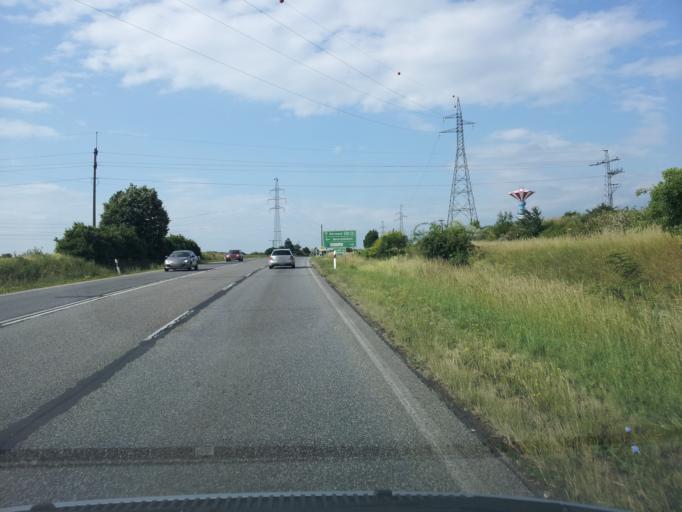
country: HU
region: Veszprem
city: Veszprem
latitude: 47.0859
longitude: 17.9298
